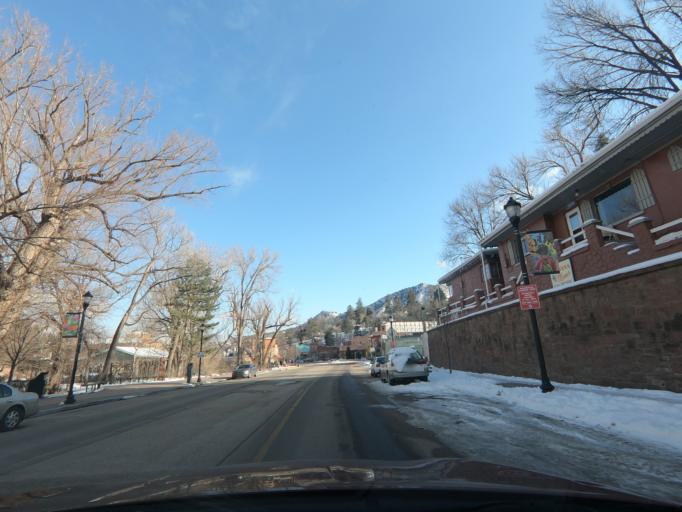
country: US
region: Colorado
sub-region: El Paso County
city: Manitou Springs
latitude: 38.8598
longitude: -104.9203
